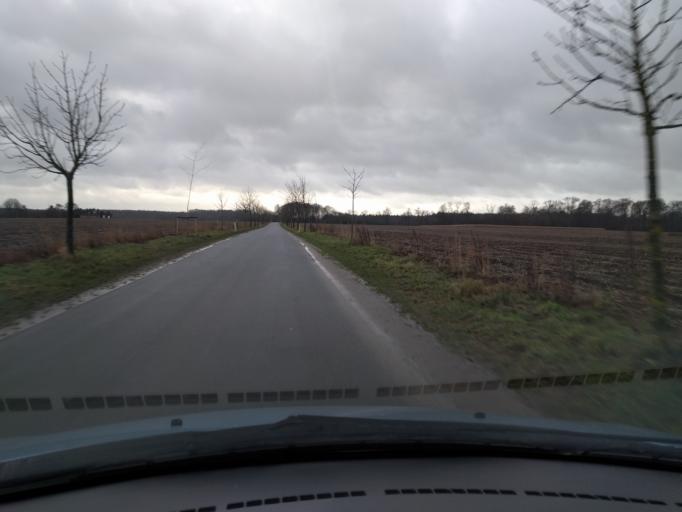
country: DK
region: South Denmark
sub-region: Kerteminde Kommune
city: Langeskov
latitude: 55.3649
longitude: 10.5612
